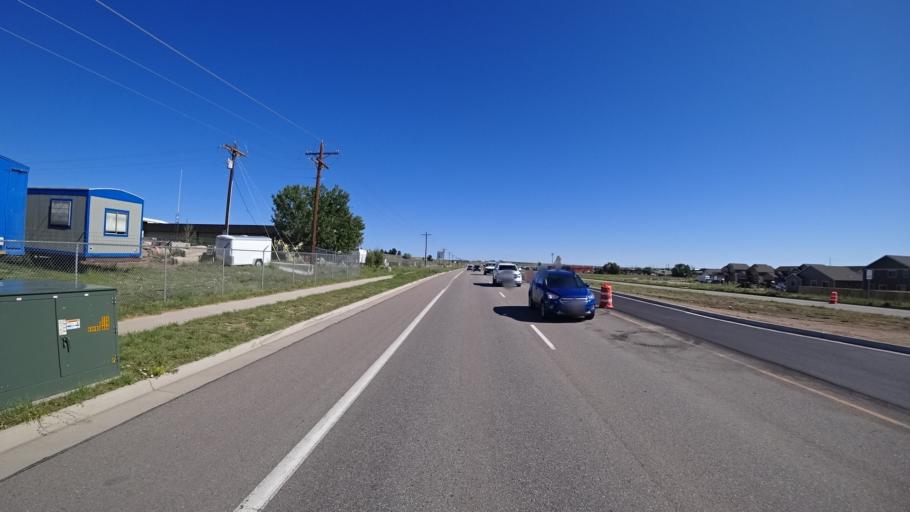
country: US
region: Colorado
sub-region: El Paso County
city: Cimarron Hills
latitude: 38.8771
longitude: -104.6829
